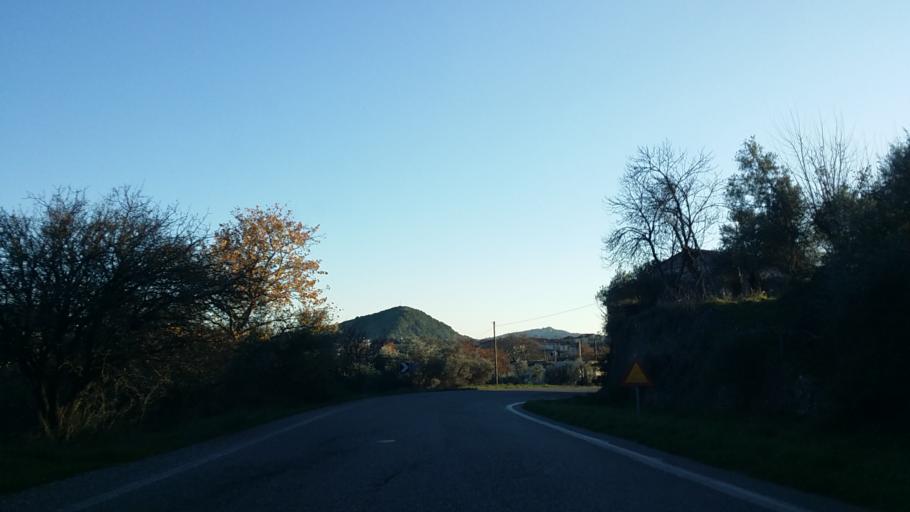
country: GR
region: West Greece
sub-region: Nomos Aitolias kai Akarnanias
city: Lepenou
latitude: 38.7422
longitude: 21.3464
